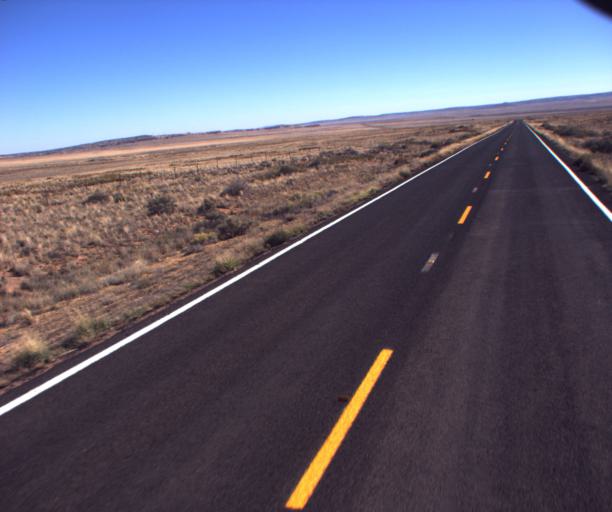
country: US
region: Arizona
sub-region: Navajo County
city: First Mesa
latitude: 35.9698
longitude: -110.8162
